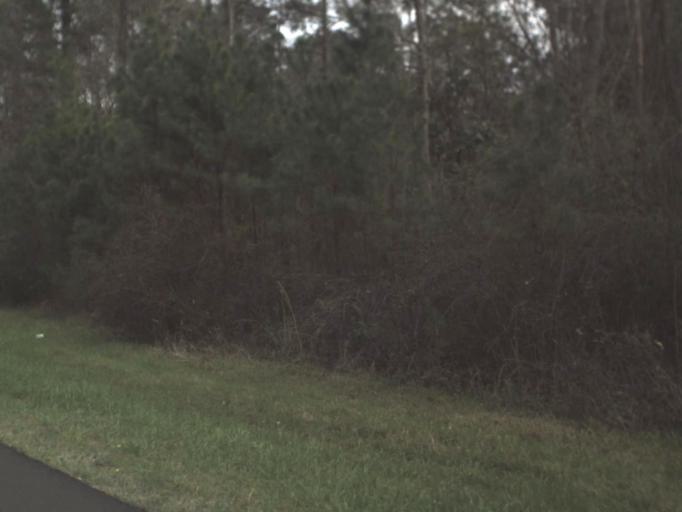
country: US
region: Florida
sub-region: Gadsden County
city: Midway
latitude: 30.3953
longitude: -84.6106
